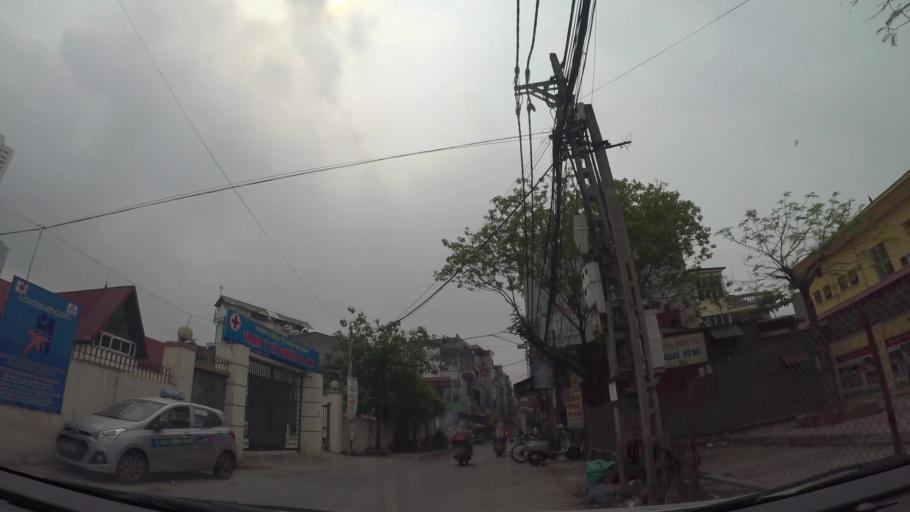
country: VN
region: Ha Noi
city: Ha Dong
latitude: 20.9656
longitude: 105.7663
